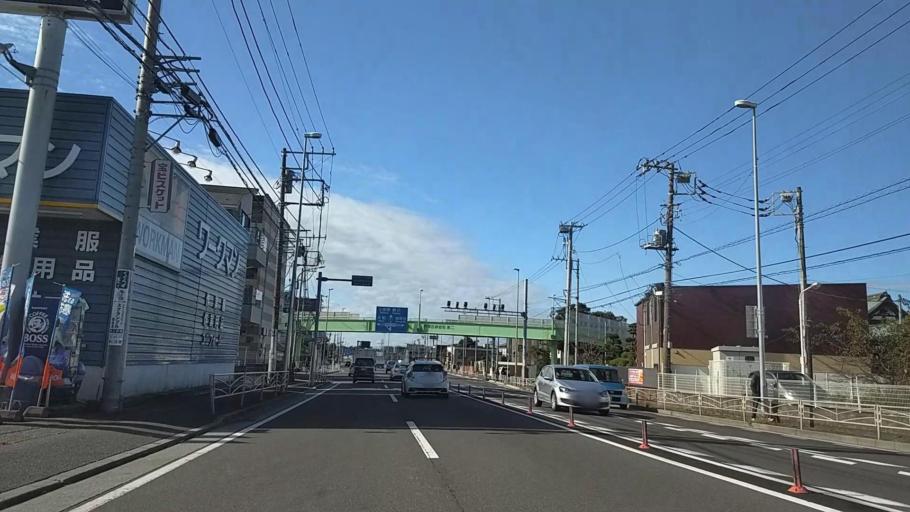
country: JP
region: Kanagawa
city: Fujisawa
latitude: 35.3792
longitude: 139.5095
